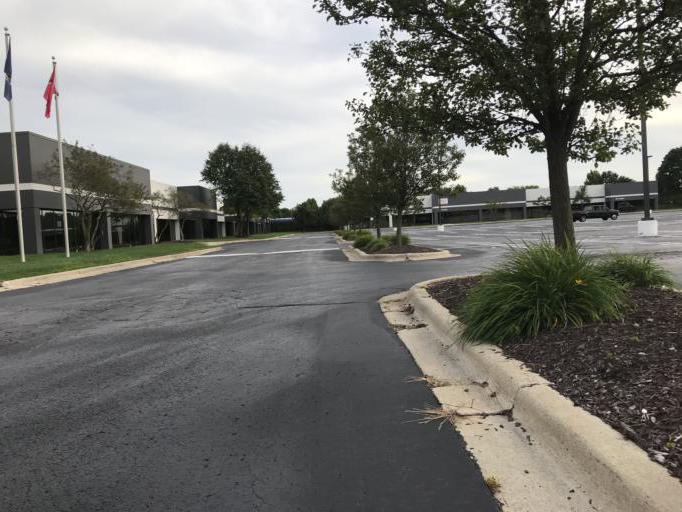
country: US
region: Michigan
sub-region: Oakland County
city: Franklin
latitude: 42.4849
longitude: -83.3176
